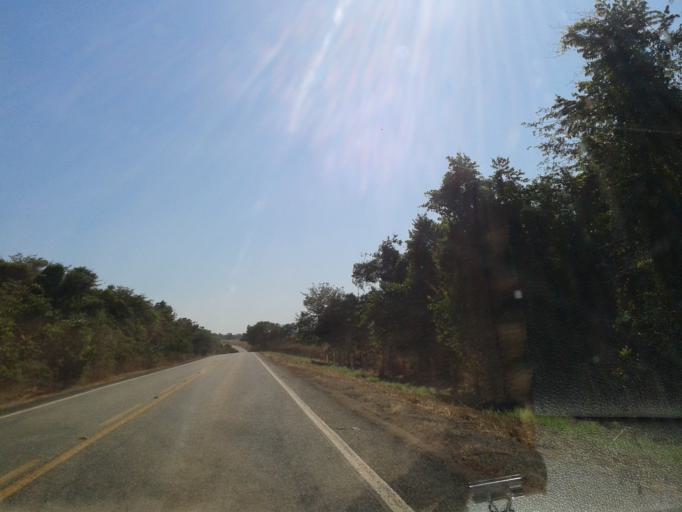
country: BR
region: Goias
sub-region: Mozarlandia
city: Mozarlandia
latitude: -14.3147
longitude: -50.4073
